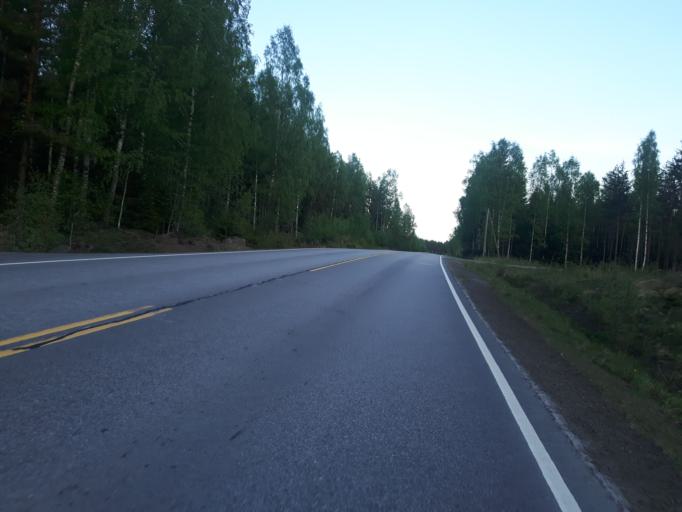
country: FI
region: Uusimaa
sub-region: Loviisa
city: Perna
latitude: 60.4574
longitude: 26.0795
